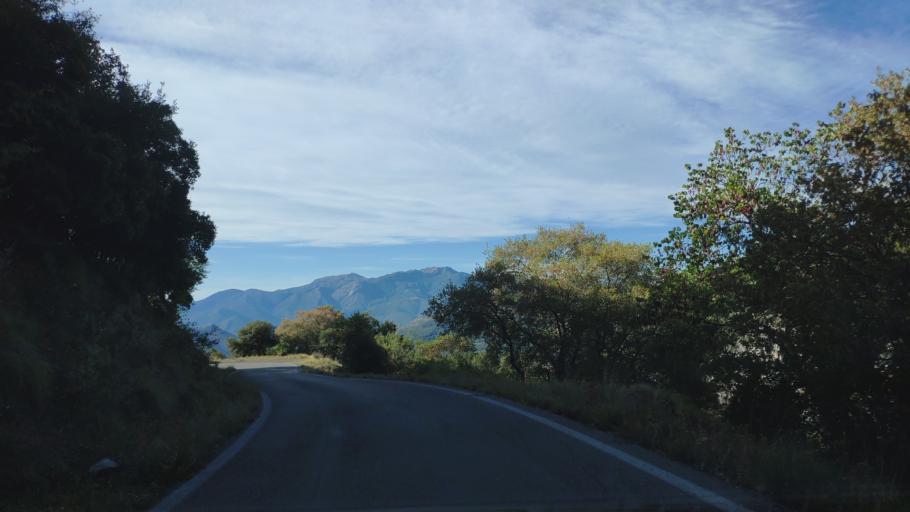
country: GR
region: Peloponnese
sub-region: Nomos Arkadias
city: Dimitsana
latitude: 37.5516
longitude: 22.0547
